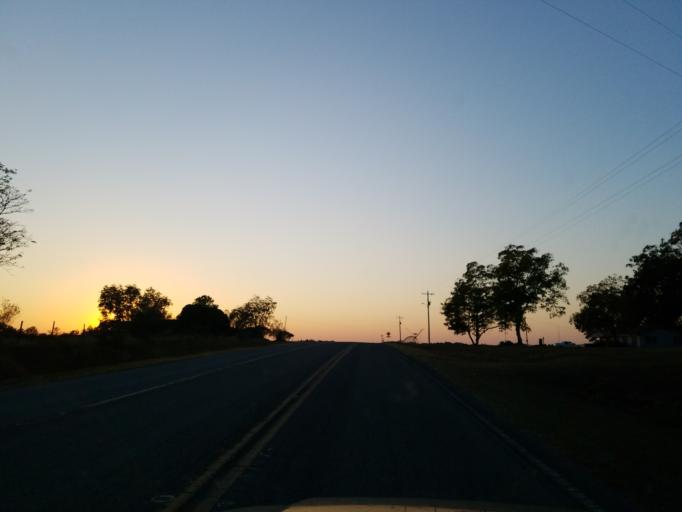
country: US
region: Georgia
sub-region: Ben Hill County
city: Fitzgerald
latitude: 31.7202
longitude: -83.4075
